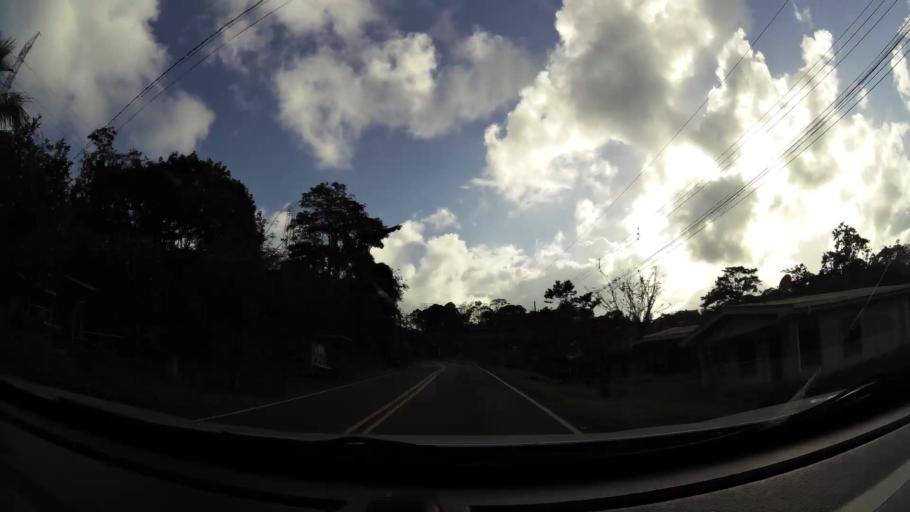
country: CR
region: Limon
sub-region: Canton de Siquirres
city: Siquirres
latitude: 10.0714
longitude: -83.5508
